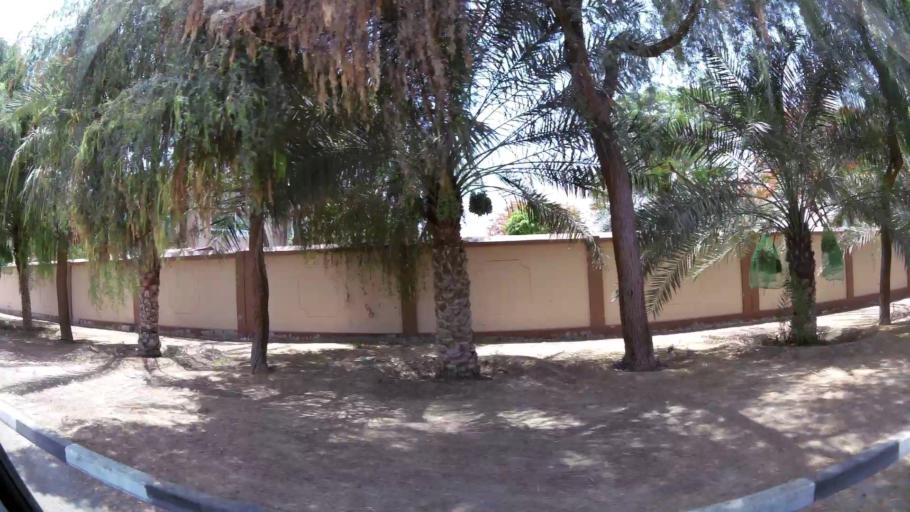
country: AE
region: Ash Shariqah
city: Sharjah
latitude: 25.2442
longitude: 55.4641
